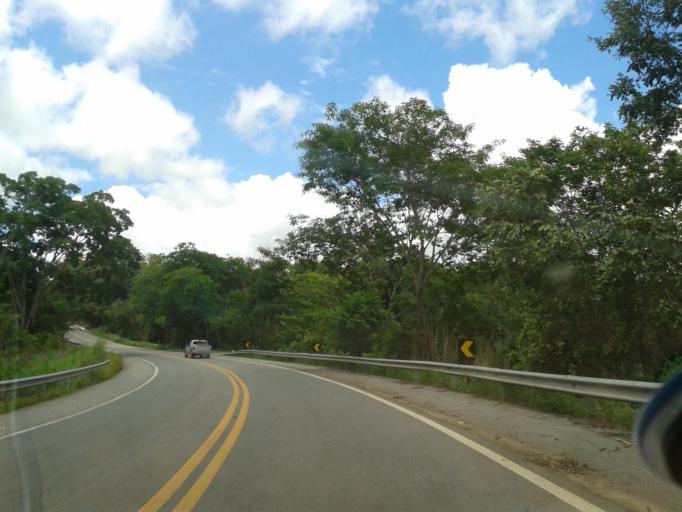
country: BR
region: Goias
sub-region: Goias
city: Goias
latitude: -15.8901
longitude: -50.1053
